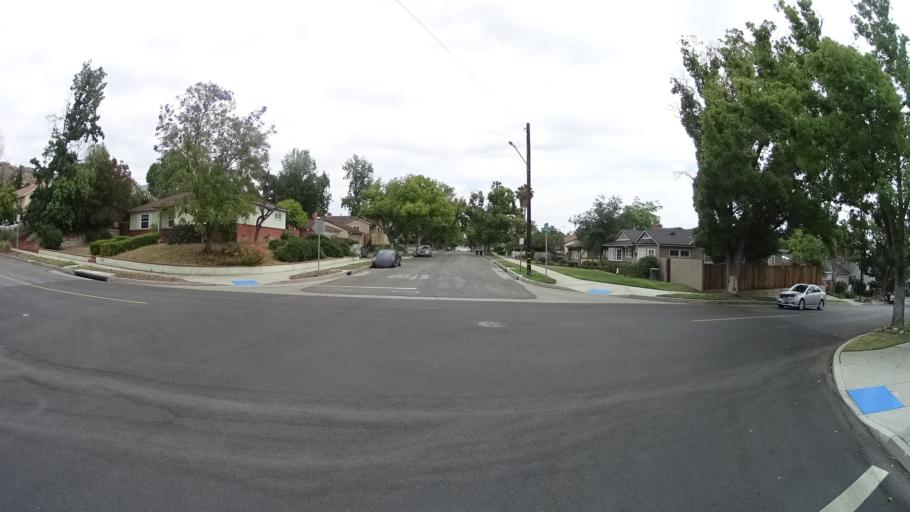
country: US
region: California
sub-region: Los Angeles County
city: Burbank
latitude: 34.2024
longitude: -118.3255
